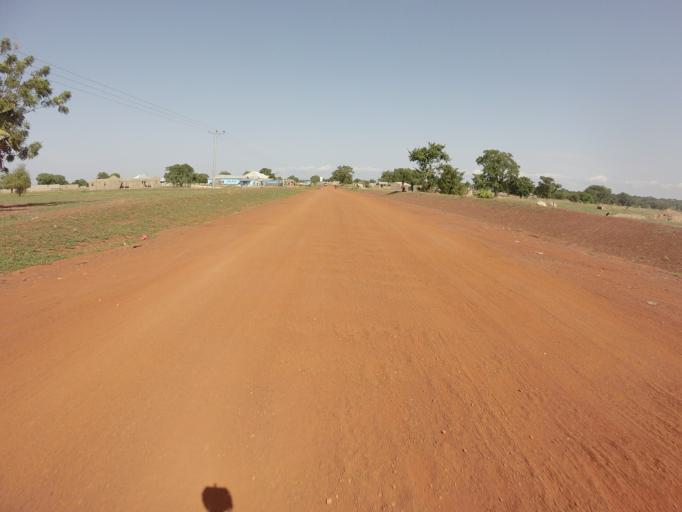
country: GH
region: Upper East
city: Bawku
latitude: 10.8325
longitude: -0.1721
